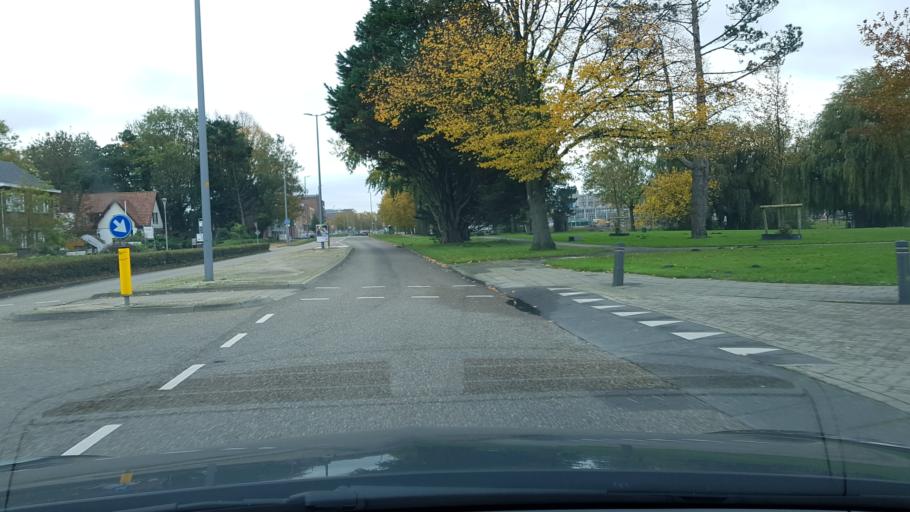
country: NL
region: North Holland
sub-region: Gemeente Haarlemmermeer
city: Hoofddorp
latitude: 52.3003
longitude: 4.7025
